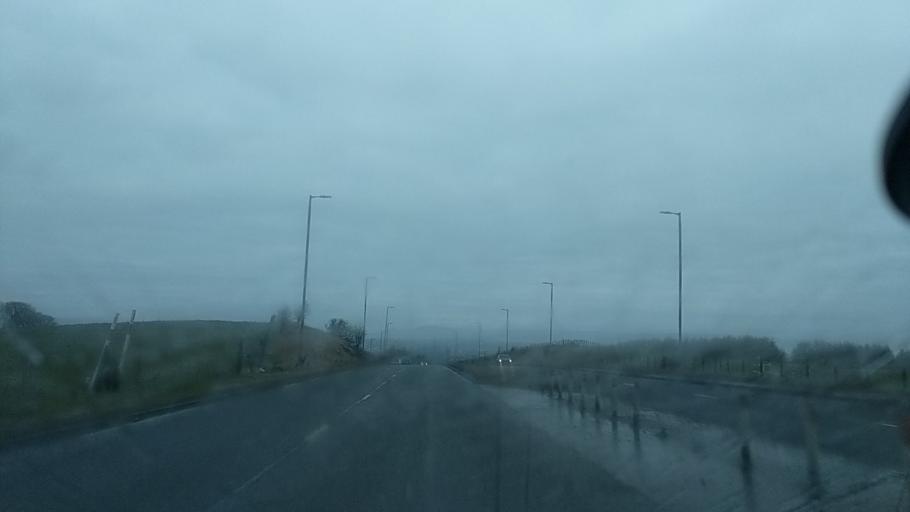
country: GB
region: Scotland
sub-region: South Lanarkshire
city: East Kilbride
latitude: 55.7948
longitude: -4.1679
